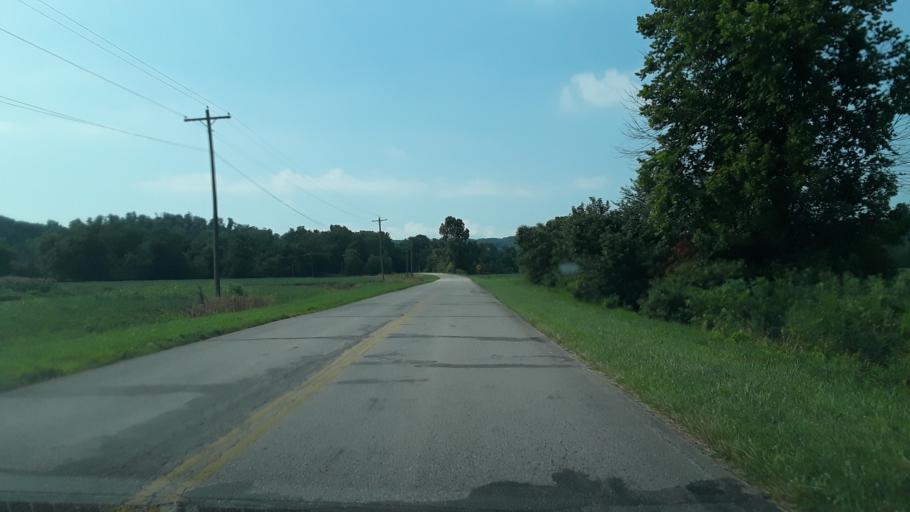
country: US
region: Indiana
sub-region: Clark County
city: Sellersburg
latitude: 38.4520
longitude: -85.8656
